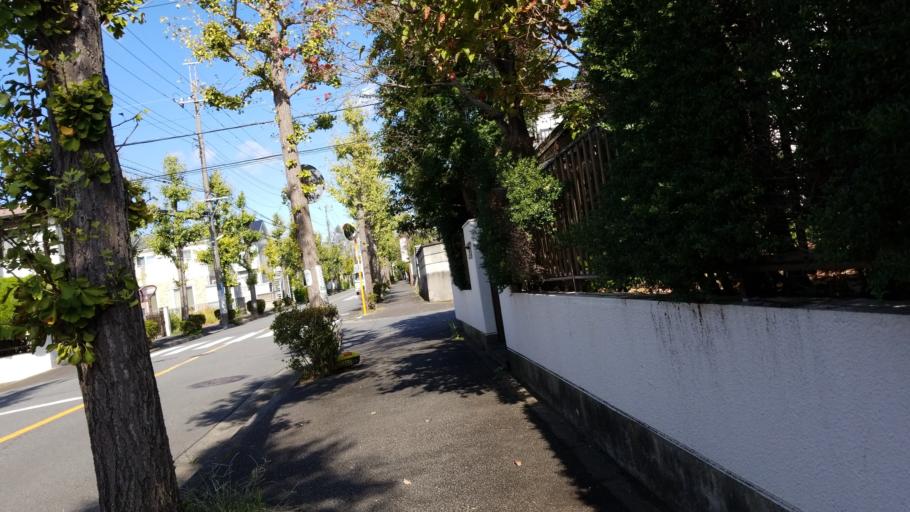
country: JP
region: Tokyo
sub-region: Machida-shi
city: Machida
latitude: 35.5894
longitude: 139.5025
